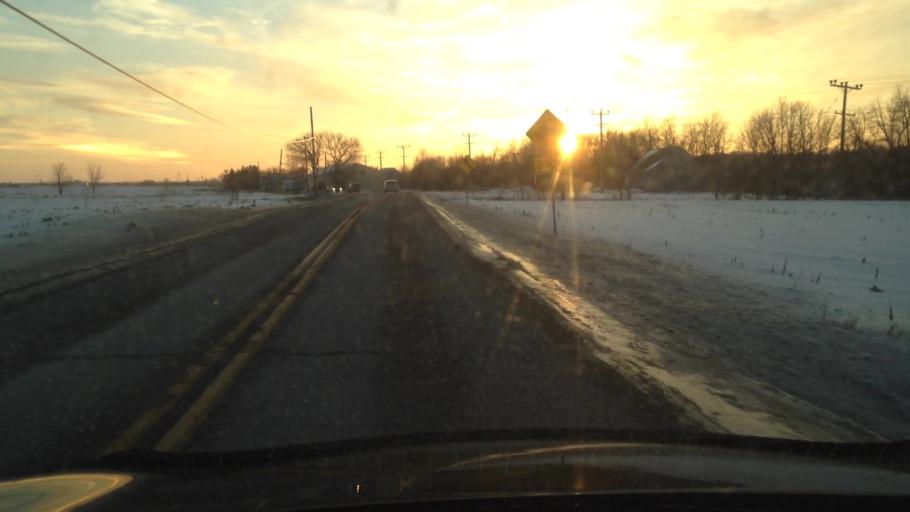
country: CA
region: Quebec
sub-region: Lanaudiere
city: Sainte-Julienne
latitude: 45.9103
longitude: -73.7421
